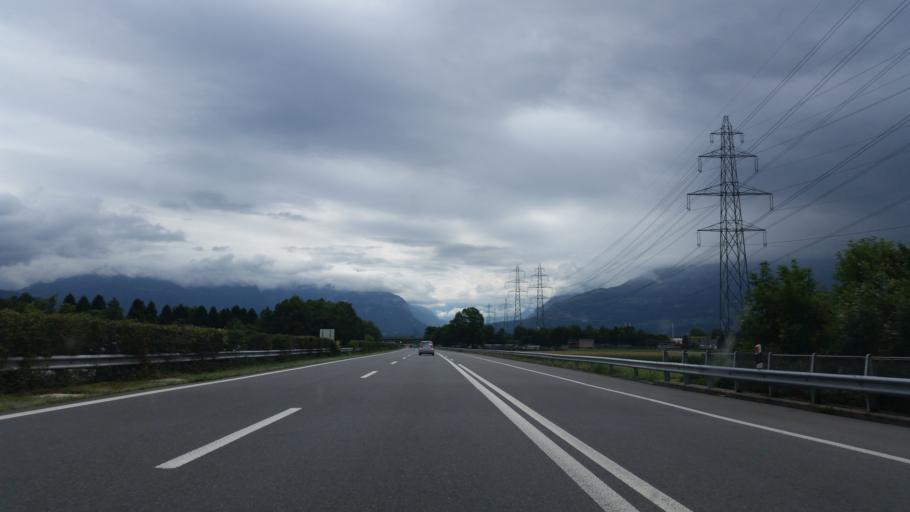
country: CH
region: Vaud
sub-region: Aigle District
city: Aigle
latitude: 46.3191
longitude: 6.9414
